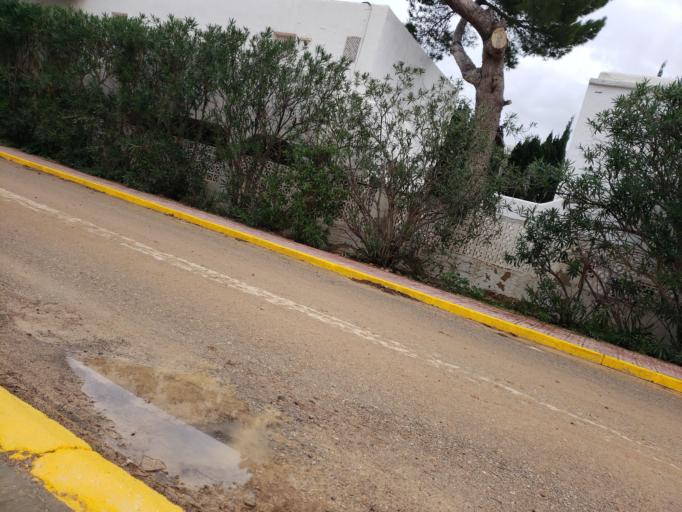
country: ES
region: Balearic Islands
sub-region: Illes Balears
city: Sant Joan de Labritja
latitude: 39.1095
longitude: 1.5097
